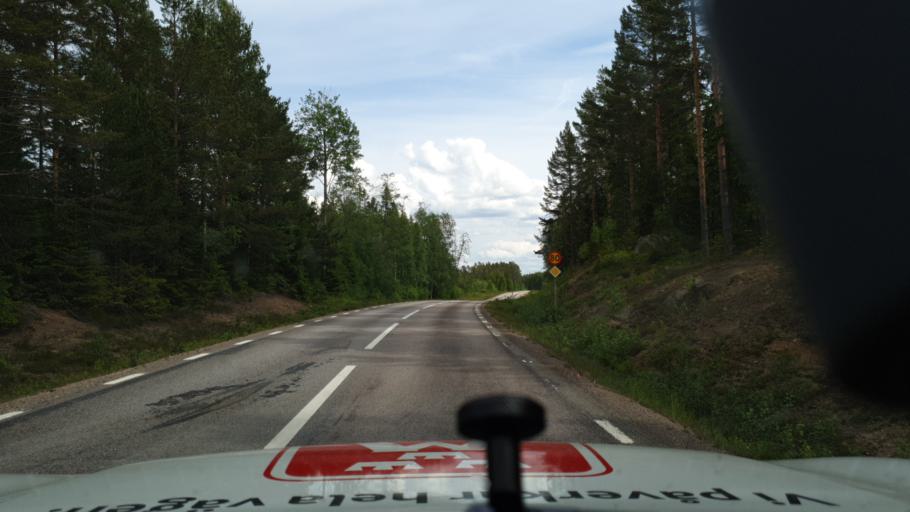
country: SE
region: Vaermland
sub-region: Torsby Kommun
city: Torsby
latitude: 60.1378
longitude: 12.8096
